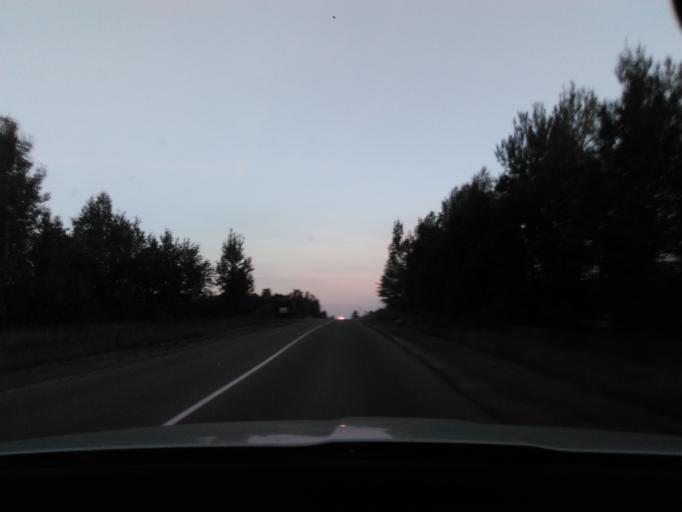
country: RU
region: Moskovskaya
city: Klin
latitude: 56.2360
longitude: 36.7513
